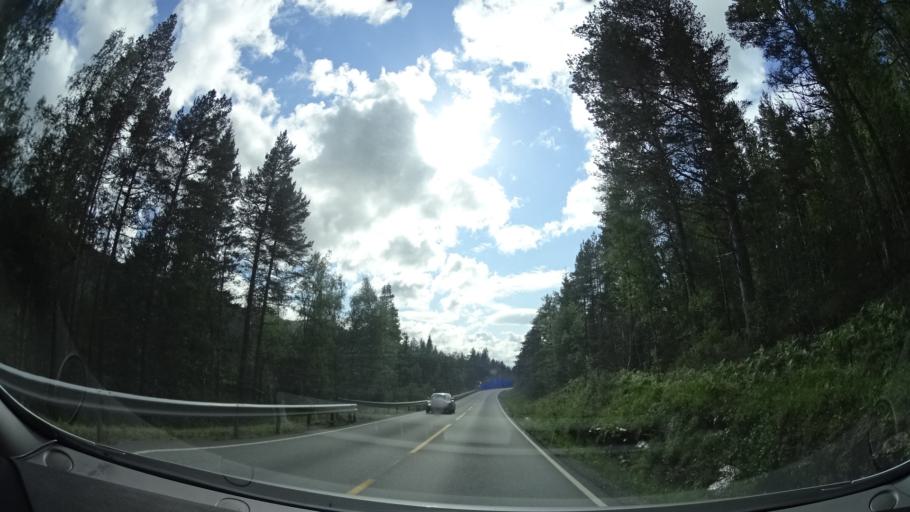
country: NO
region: Sor-Trondelag
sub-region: Hemne
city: Kyrksaeterora
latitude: 63.2117
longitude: 9.0998
